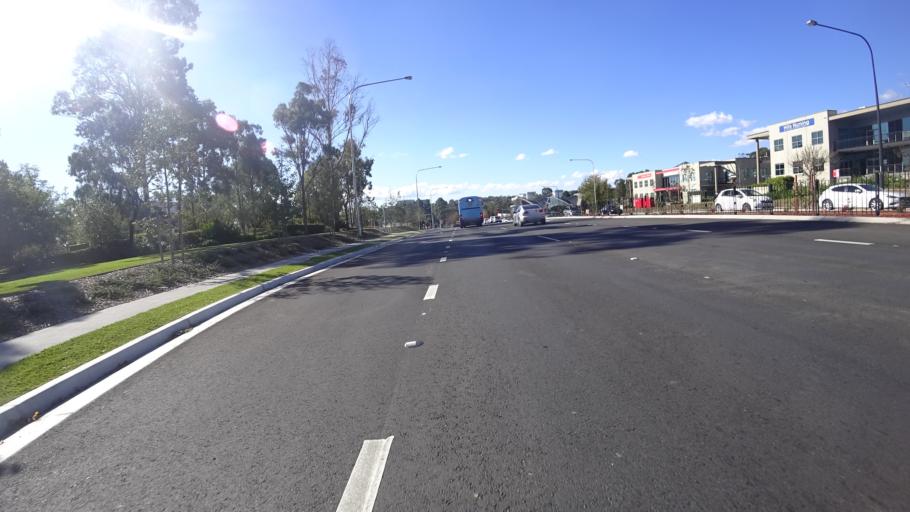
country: AU
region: New South Wales
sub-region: The Hills Shire
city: Castle Hill
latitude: -33.7355
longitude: 150.9618
